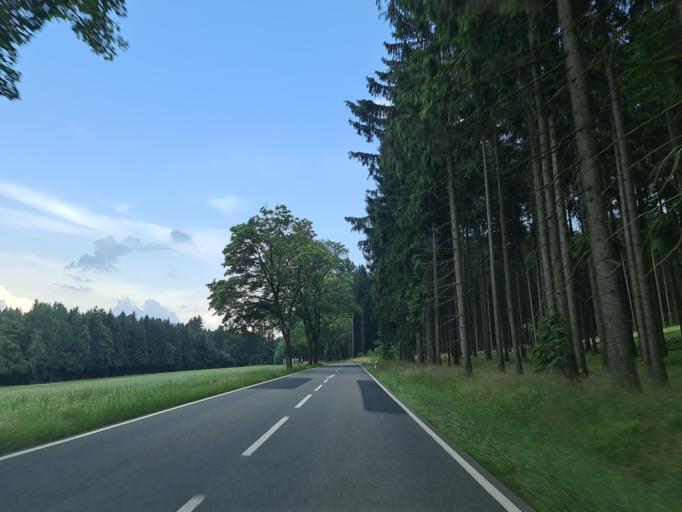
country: DE
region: Saxony
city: Neustadt Vogtland
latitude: 50.4601
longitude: 12.3028
